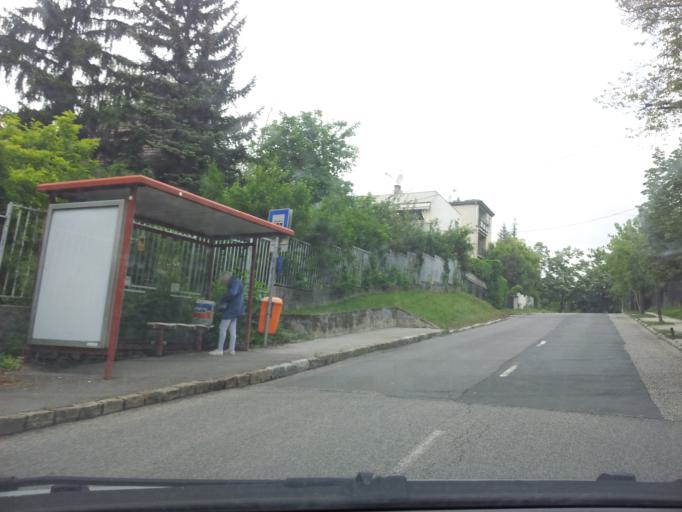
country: HU
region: Budapest
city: Budapest XII. keruelet
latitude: 47.5092
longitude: 18.9996
